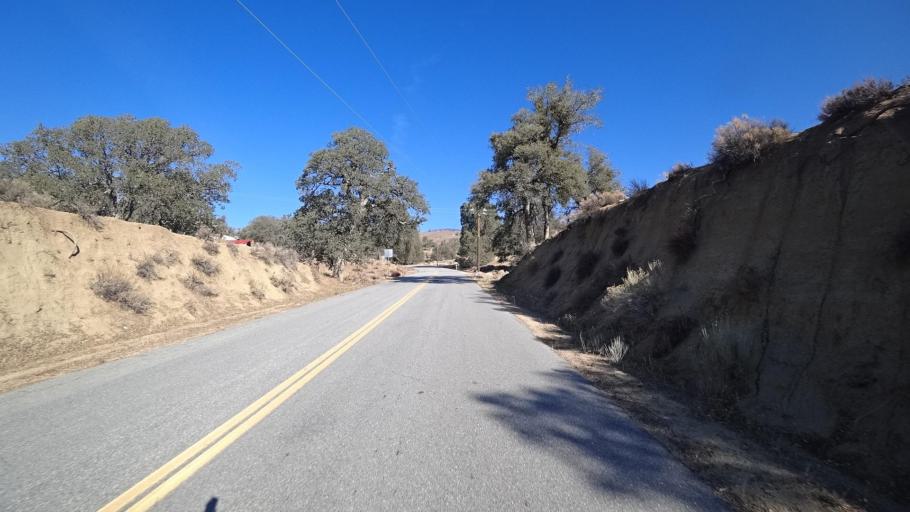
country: US
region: California
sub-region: Kern County
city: Bodfish
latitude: 35.3760
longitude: -118.4001
